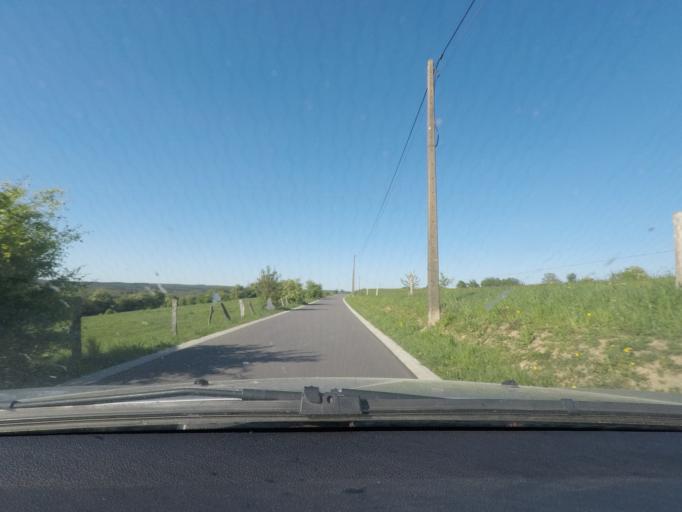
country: BE
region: Wallonia
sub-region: Province du Luxembourg
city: Tintigny
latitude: 49.6989
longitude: 5.4459
